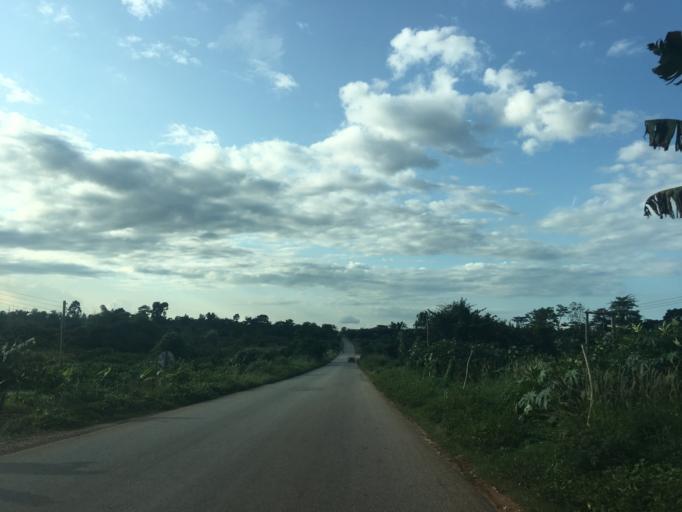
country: GH
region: Western
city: Bibiani
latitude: 6.3074
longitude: -2.2505
